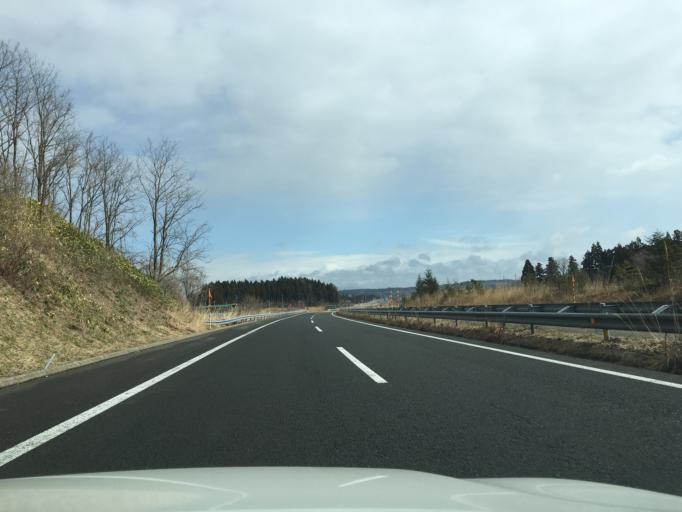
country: JP
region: Akita
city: Akita
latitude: 39.6113
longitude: 140.1396
